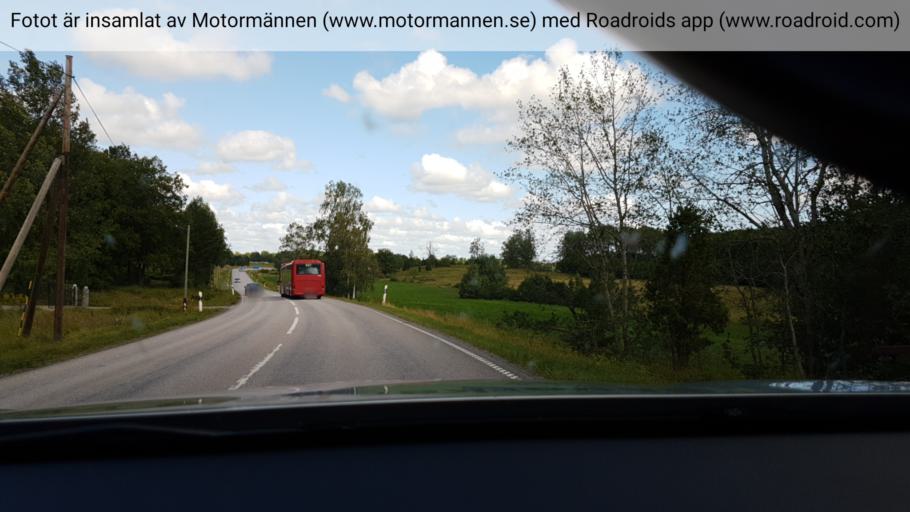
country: SE
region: Stockholm
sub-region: Norrtalje Kommun
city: Norrtalje
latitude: 59.8751
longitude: 18.7013
